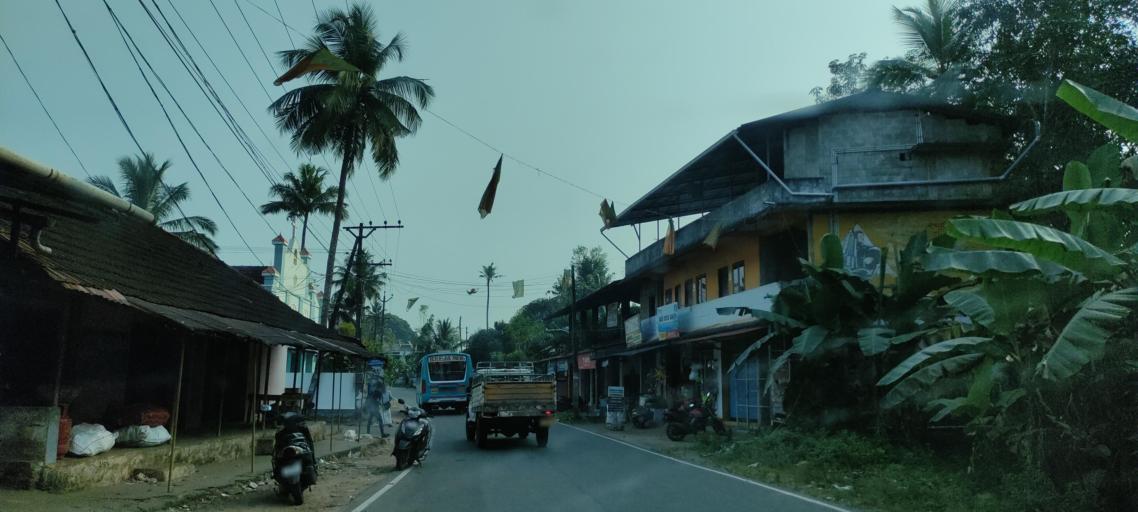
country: IN
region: Kerala
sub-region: Pattanamtitta
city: Adur
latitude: 9.1207
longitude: 76.7307
